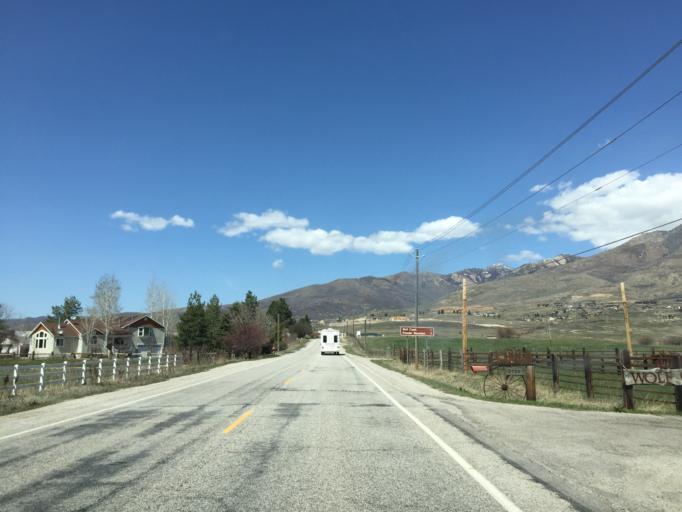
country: US
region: Utah
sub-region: Weber County
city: Wolf Creek
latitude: 41.3080
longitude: -111.8253
